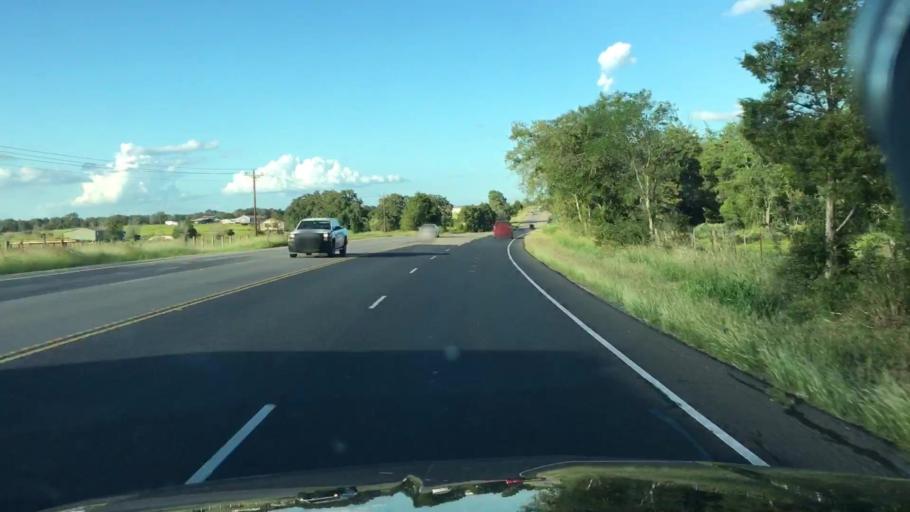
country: US
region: Texas
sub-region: Bastrop County
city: Camp Swift
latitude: 30.1959
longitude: -97.1611
